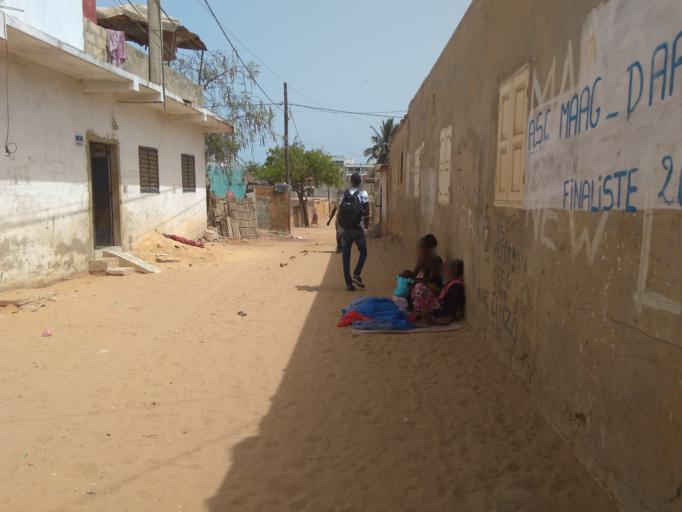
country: SN
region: Dakar
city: Pikine
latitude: 14.7921
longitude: -17.3375
